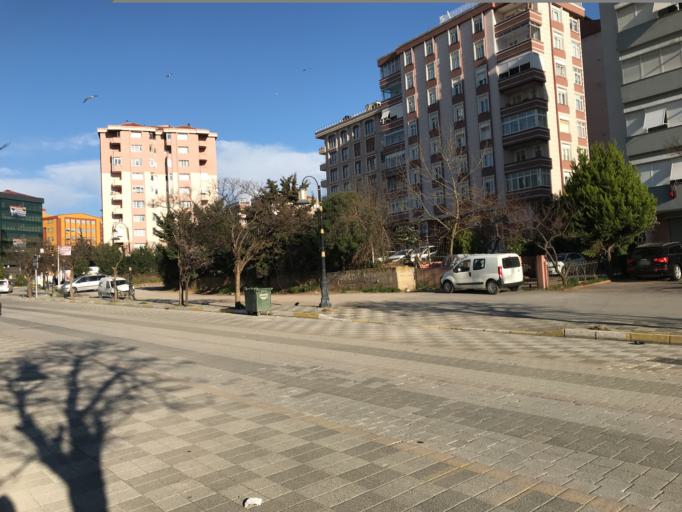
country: TR
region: Istanbul
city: Maltepe
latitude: 40.9325
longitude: 29.1334
